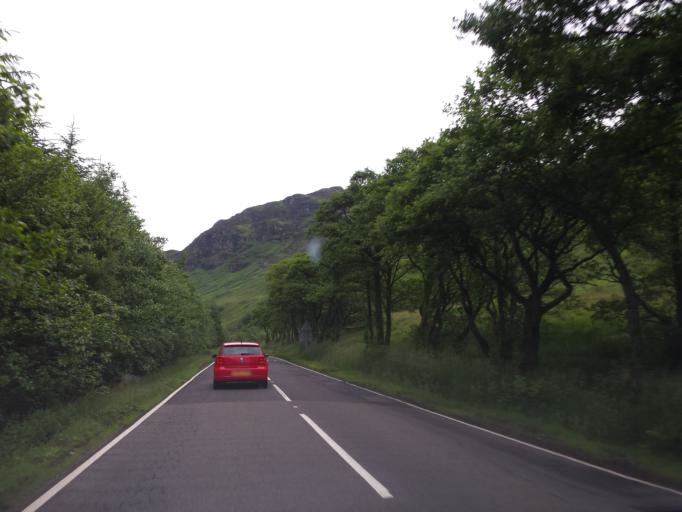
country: GB
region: Scotland
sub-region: Stirling
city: Callander
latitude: 56.4023
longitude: -4.3035
